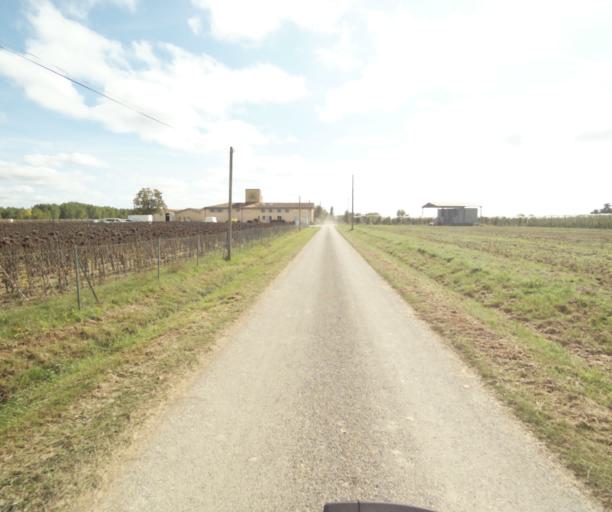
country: FR
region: Midi-Pyrenees
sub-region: Departement du Tarn-et-Garonne
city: Montech
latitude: 43.9432
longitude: 1.2060
